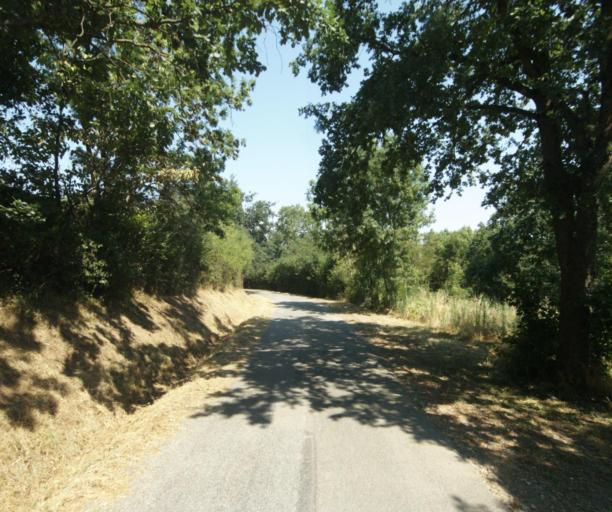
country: FR
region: Rhone-Alpes
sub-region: Departement du Rhone
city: Saint-Pierre-la-Palud
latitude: 45.7976
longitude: 4.6066
